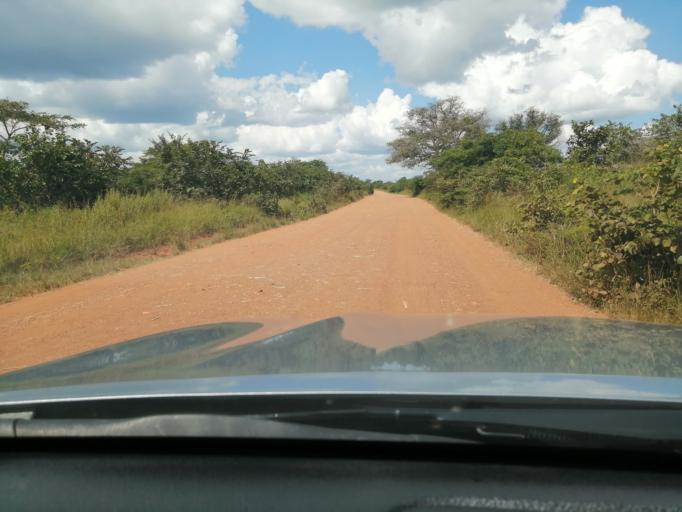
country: ZM
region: Lusaka
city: Lusaka
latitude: -15.1999
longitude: 28.0179
